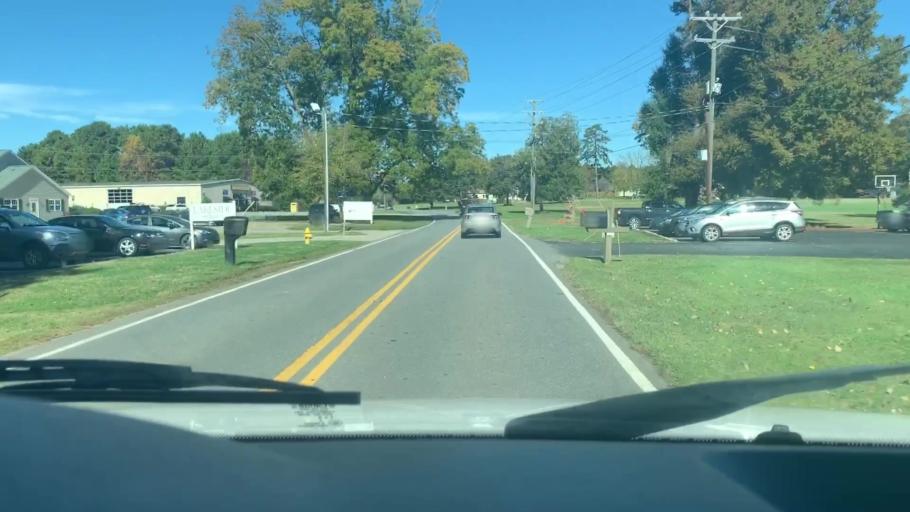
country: US
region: North Carolina
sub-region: Lincoln County
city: Lowesville
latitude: 35.4510
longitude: -80.9903
